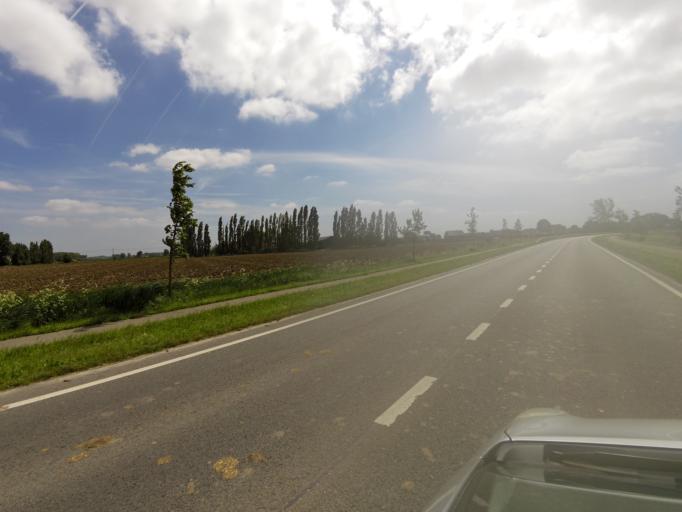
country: BE
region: Flanders
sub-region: Provincie West-Vlaanderen
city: Diksmuide
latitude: 51.0919
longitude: 2.8870
